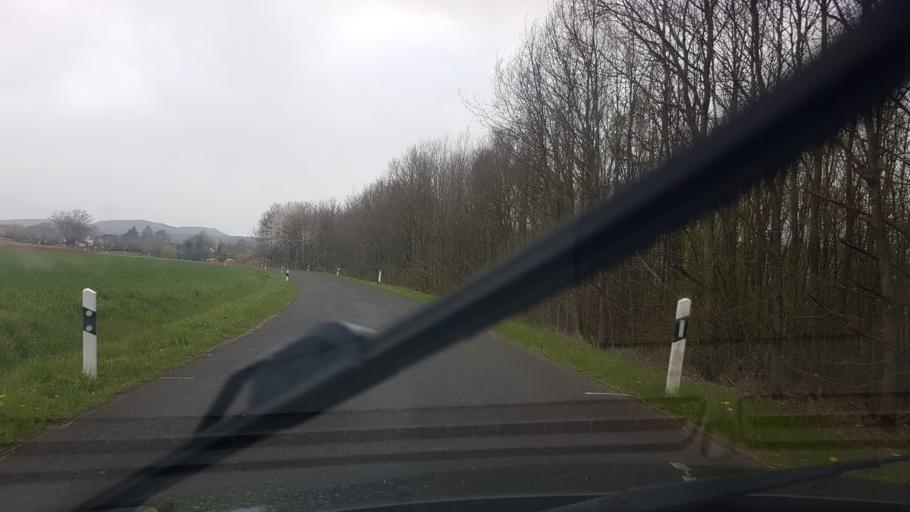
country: DE
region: Bavaria
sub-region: Upper Franconia
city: Reckendorf
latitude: 50.0264
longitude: 10.8401
